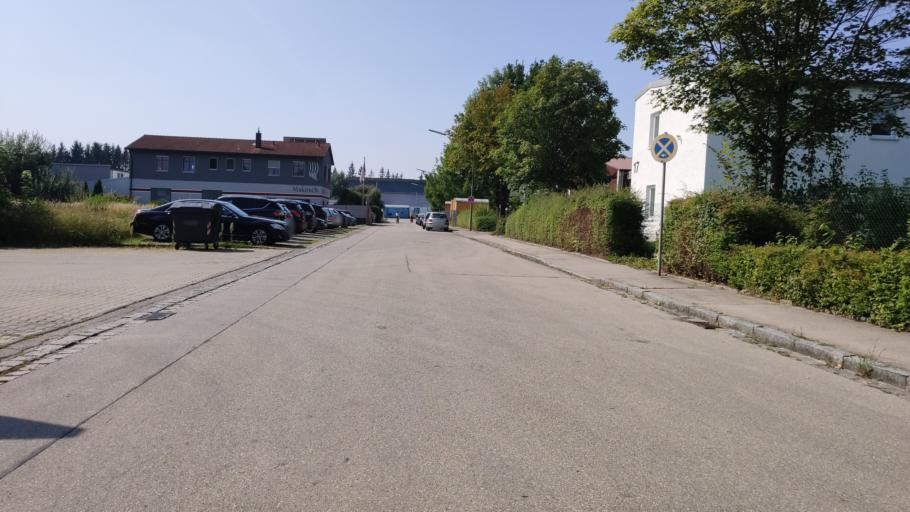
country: DE
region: Bavaria
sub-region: Swabia
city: Bobingen
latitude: 48.2687
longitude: 10.8422
